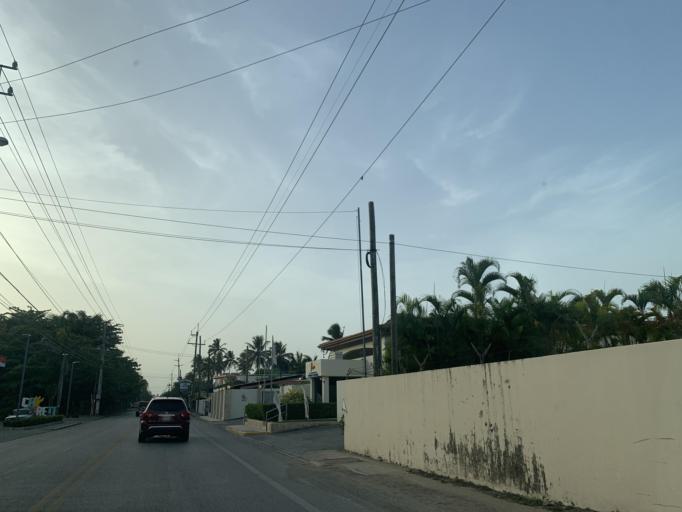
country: DO
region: Puerto Plata
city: Cabarete
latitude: 19.7527
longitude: -70.4165
